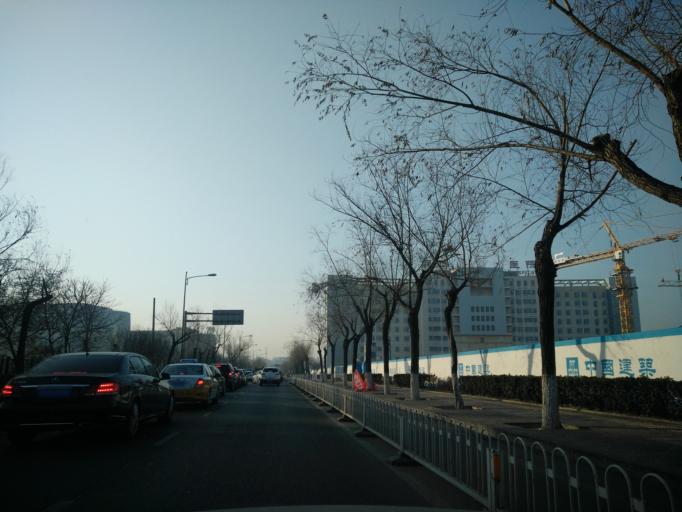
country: CN
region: Beijing
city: Jiugong
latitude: 39.7750
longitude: 116.5161
